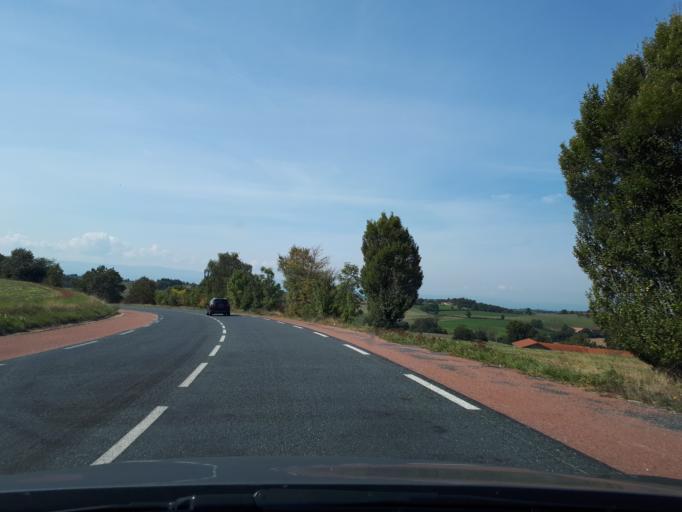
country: FR
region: Rhone-Alpes
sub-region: Departement du Rhone
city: Haute-Rivoire
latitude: 45.7289
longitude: 4.3989
